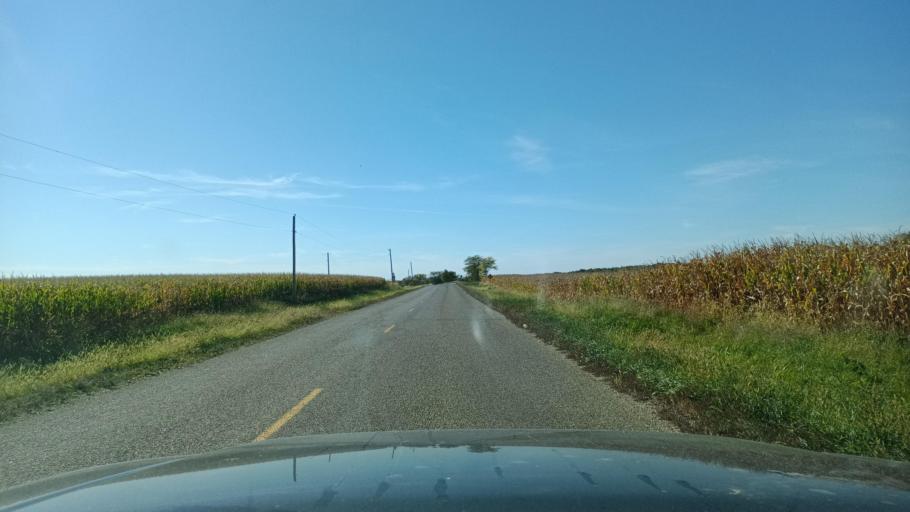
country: US
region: Illinois
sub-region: Logan County
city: Atlanta
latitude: 40.2345
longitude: -89.1457
